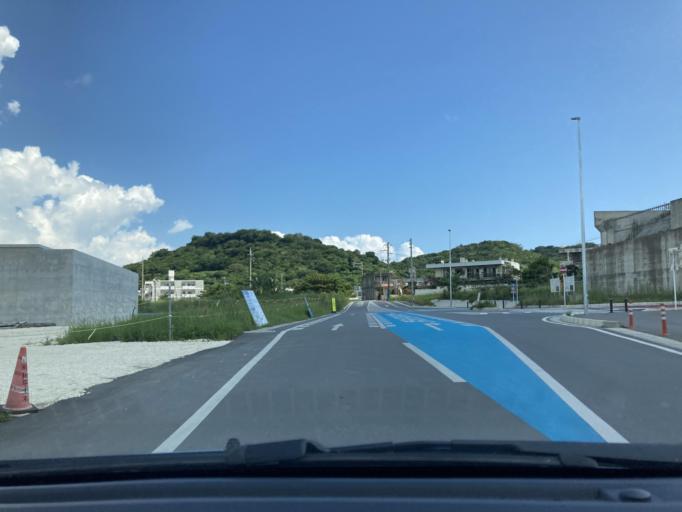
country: JP
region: Okinawa
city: Tomigusuku
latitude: 26.1606
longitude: 127.7559
